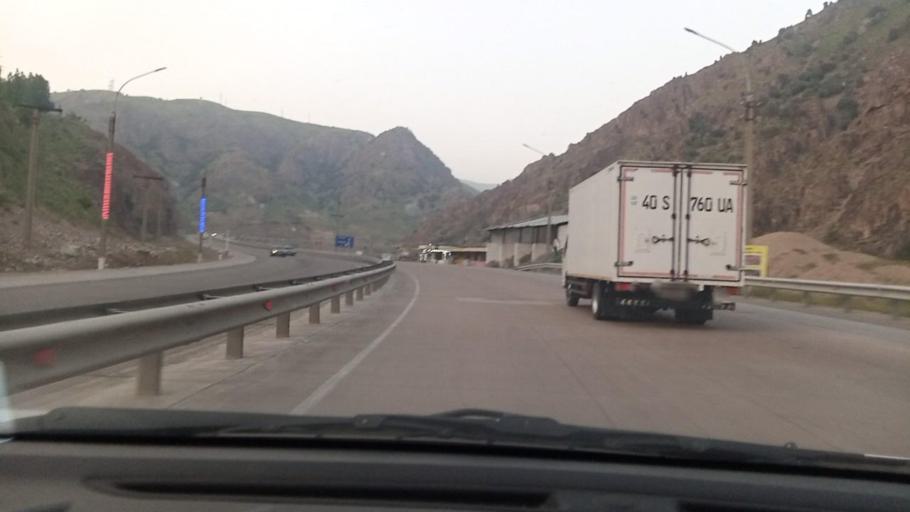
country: UZ
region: Toshkent
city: Angren
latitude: 41.1276
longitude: 70.3699
